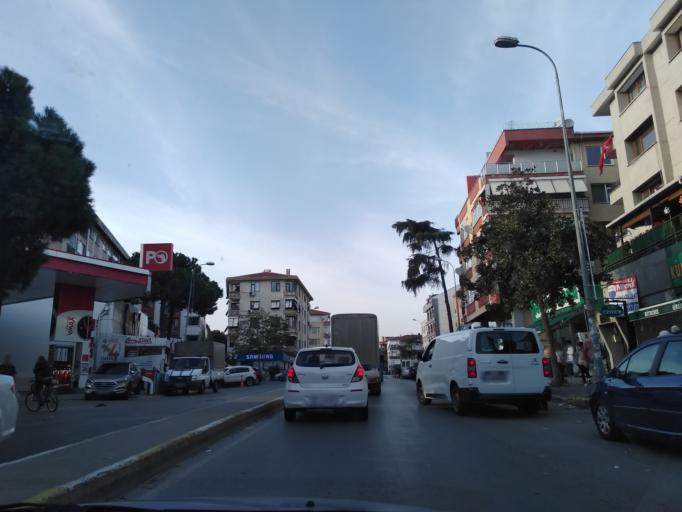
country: TR
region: Istanbul
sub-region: Atasehir
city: Atasehir
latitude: 40.9478
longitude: 29.1069
